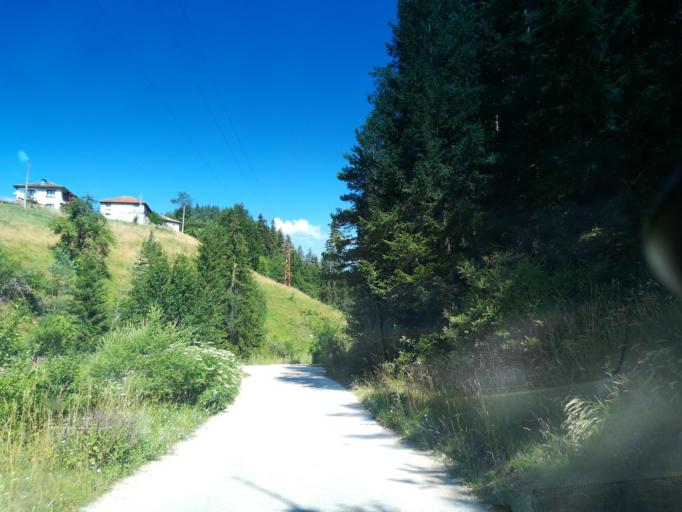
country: BG
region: Smolyan
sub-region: Obshtina Smolyan
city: Smolyan
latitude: 41.6592
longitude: 24.8185
